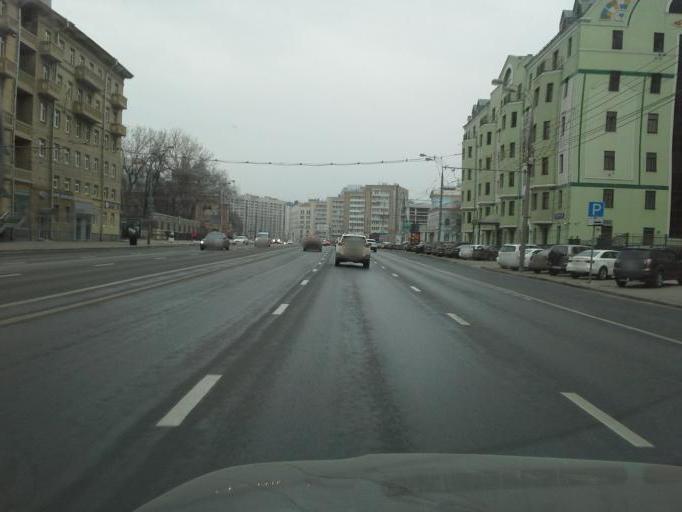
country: RU
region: Moscow
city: Moscow
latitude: 55.7346
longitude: 37.6130
